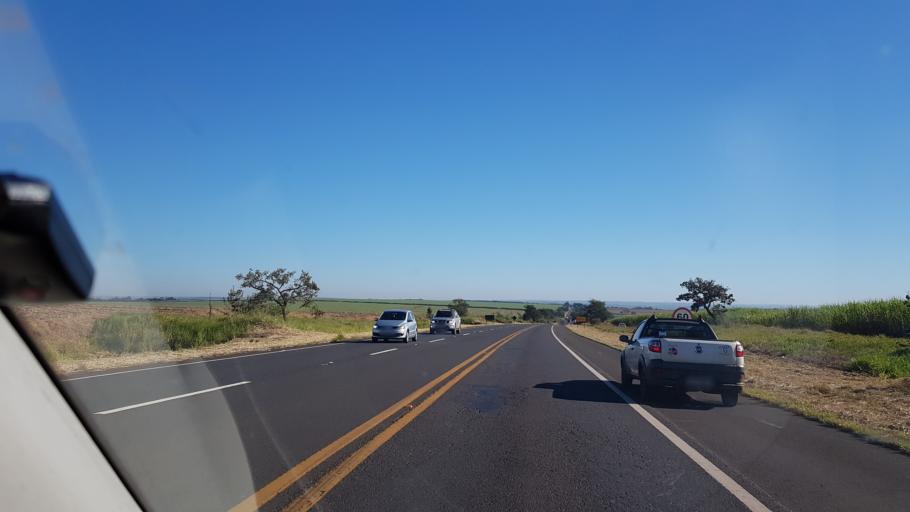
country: BR
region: Sao Paulo
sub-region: Assis
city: Assis
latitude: -22.5656
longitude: -50.5231
